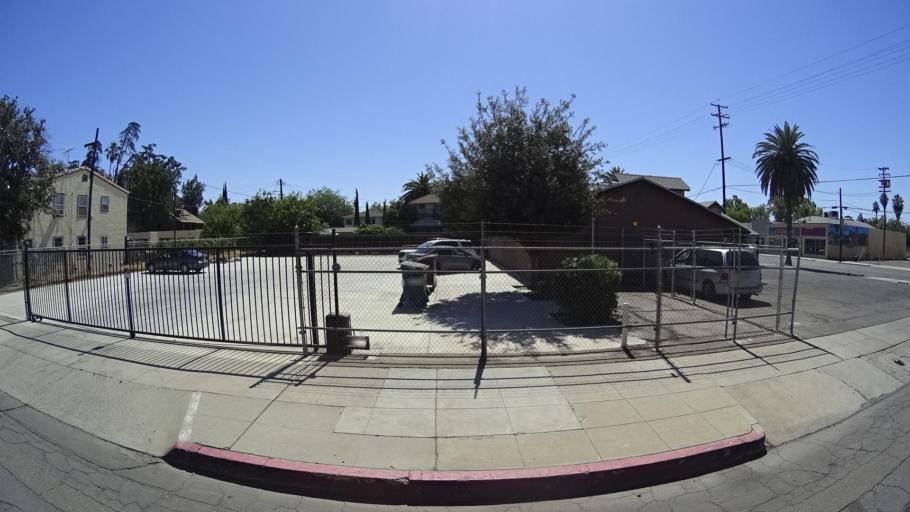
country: US
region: California
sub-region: Fresno County
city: Fresno
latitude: 36.7507
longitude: -119.8028
